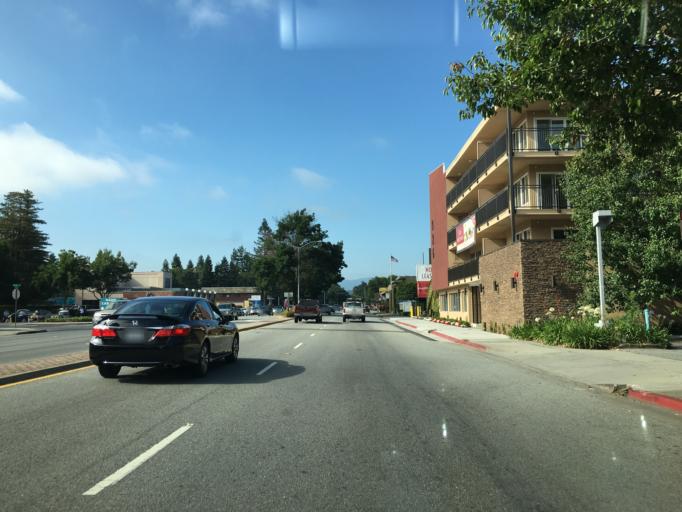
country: US
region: California
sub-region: San Mateo County
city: Redwood City
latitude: 37.4649
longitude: -122.2247
